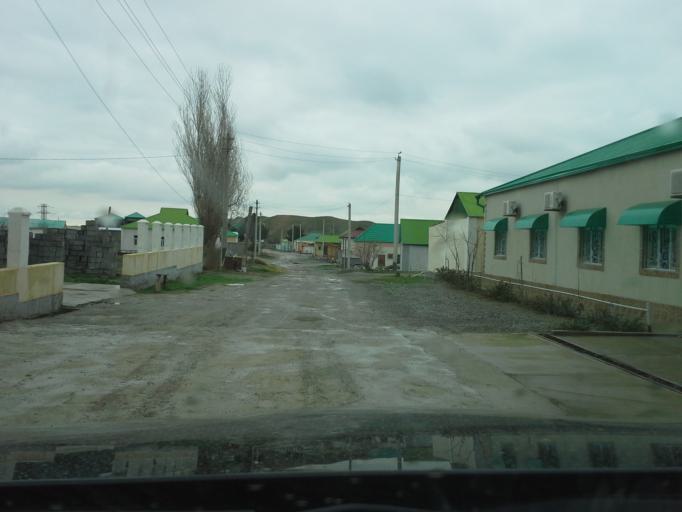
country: TM
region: Ahal
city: Abadan
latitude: 37.9482
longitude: 58.2035
